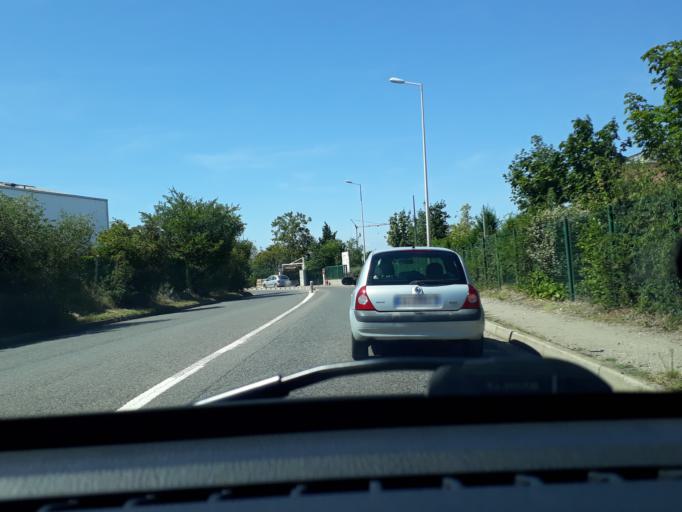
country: FR
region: Rhone-Alpes
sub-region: Departement du Rhone
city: Saint-Priest
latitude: 45.6949
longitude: 4.9228
